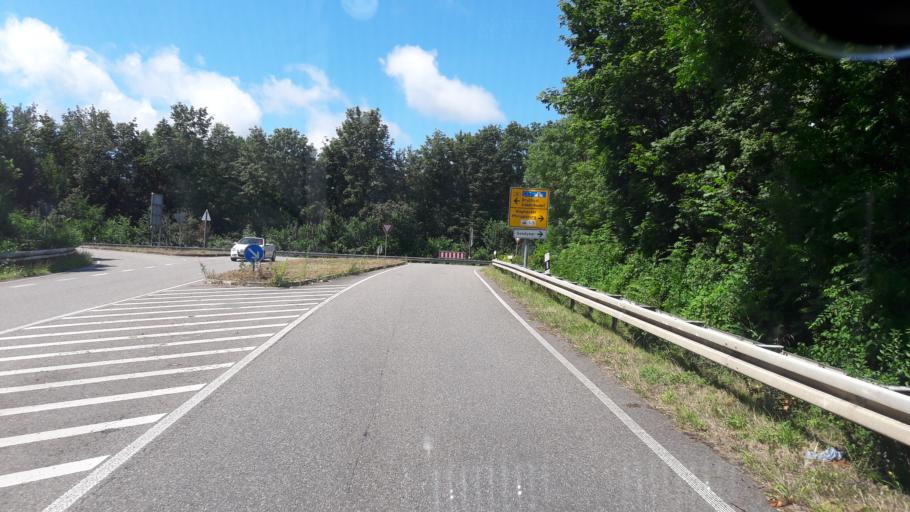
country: DE
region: Baden-Wuerttemberg
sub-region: Karlsruhe Region
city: Philippsburg
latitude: 49.1976
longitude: 8.4550
